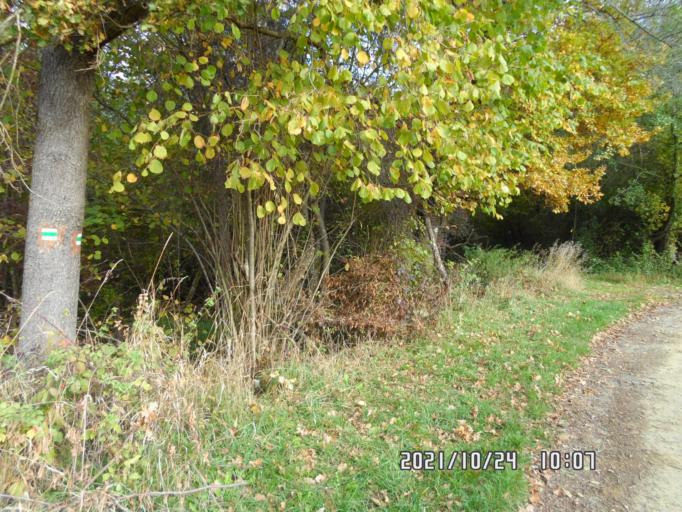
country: SI
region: Hodos-Hodos
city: Hodos
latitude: 46.8259
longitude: 16.3509
